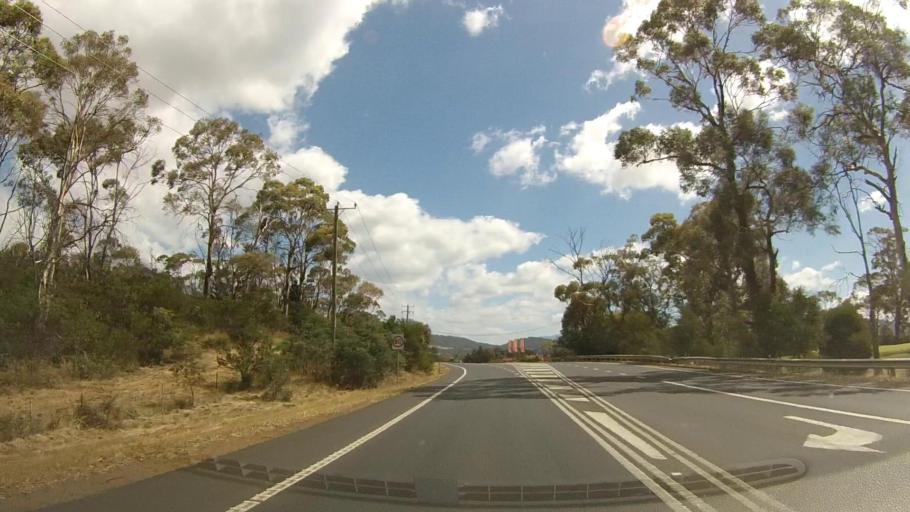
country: AU
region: Tasmania
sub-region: Clarence
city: Seven Mile Beach
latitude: -42.8220
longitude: 147.5035
